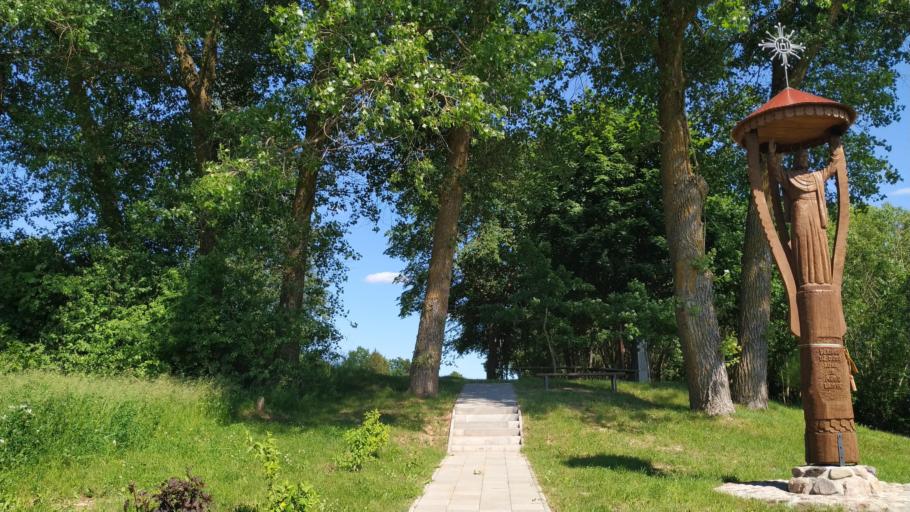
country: LT
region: Utenos apskritis
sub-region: Anyksciai
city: Anyksciai
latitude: 55.2960
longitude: 25.1167
